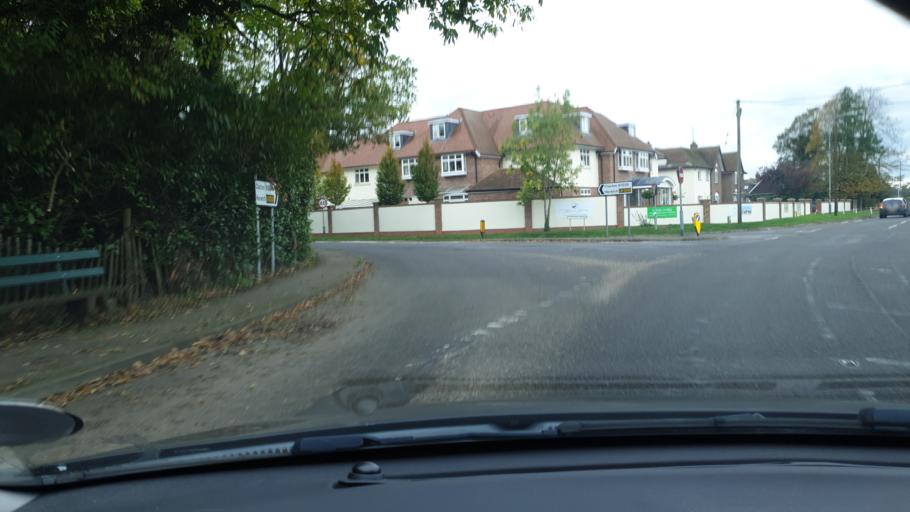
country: GB
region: England
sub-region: Essex
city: Manningtree
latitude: 51.9399
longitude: 1.0630
